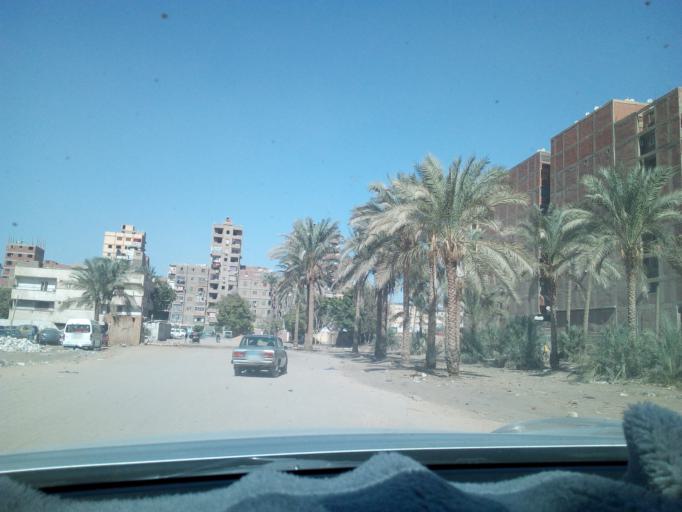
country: EG
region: Muhafazat al Qalyubiyah
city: Al Khankah
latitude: 30.1402
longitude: 31.3346
